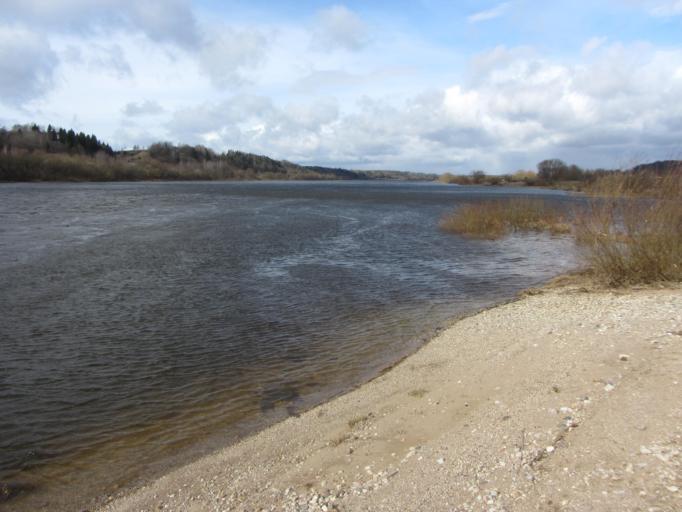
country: LT
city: Kulautuva
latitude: 54.9410
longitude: 23.6297
